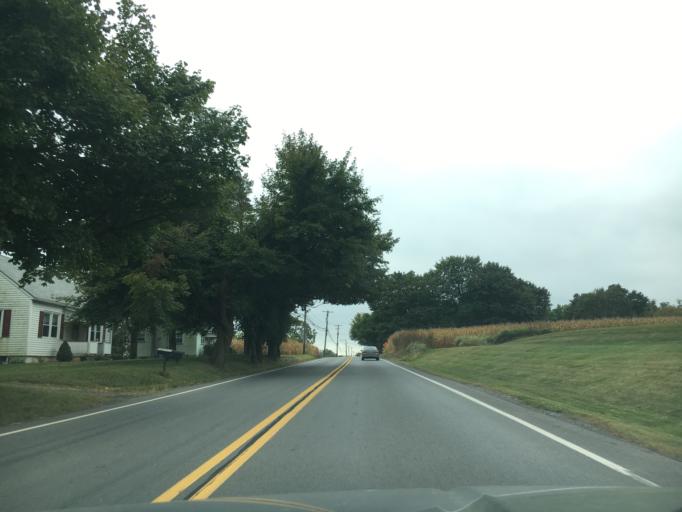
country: US
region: Pennsylvania
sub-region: Northampton County
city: Bath
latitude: 40.6966
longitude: -75.3924
